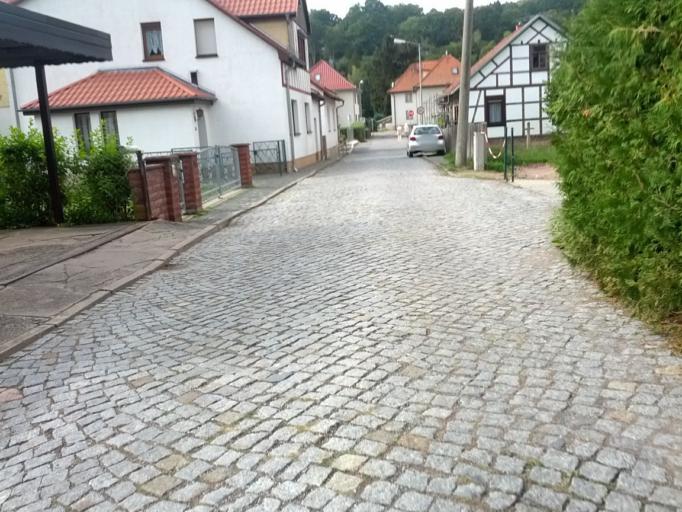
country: DE
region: Thuringia
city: Thal
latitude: 50.9374
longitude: 10.3934
